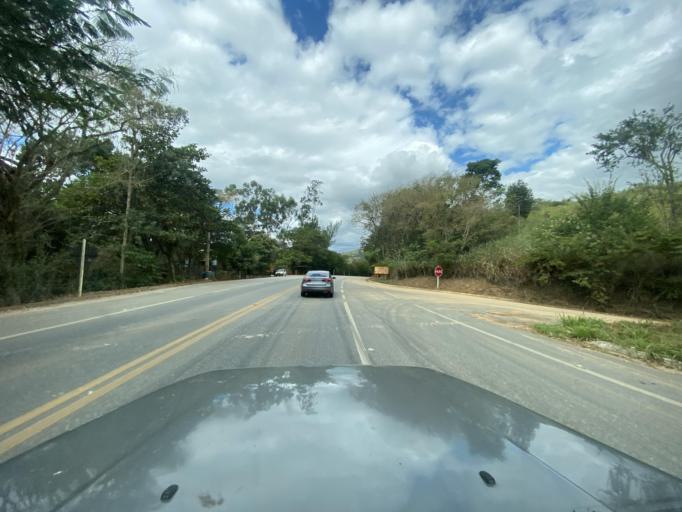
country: BR
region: Espirito Santo
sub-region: Jeronimo Monteiro
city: Jeronimo Monteiro
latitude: -20.7818
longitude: -41.4136
